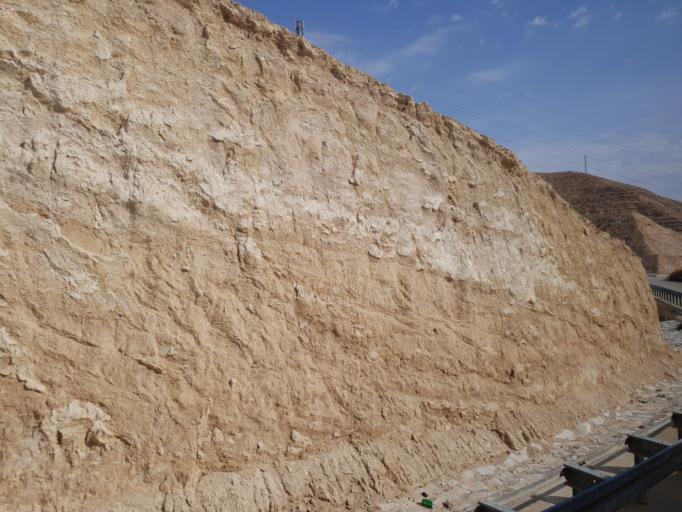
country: PS
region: West Bank
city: Jericho
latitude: 31.8014
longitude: 35.4030
